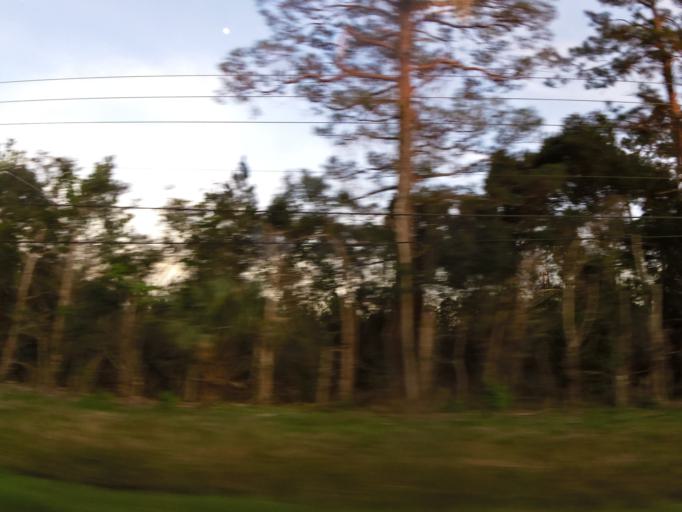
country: US
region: Florida
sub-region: Volusia County
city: North DeLand
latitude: 29.0838
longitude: -81.3047
